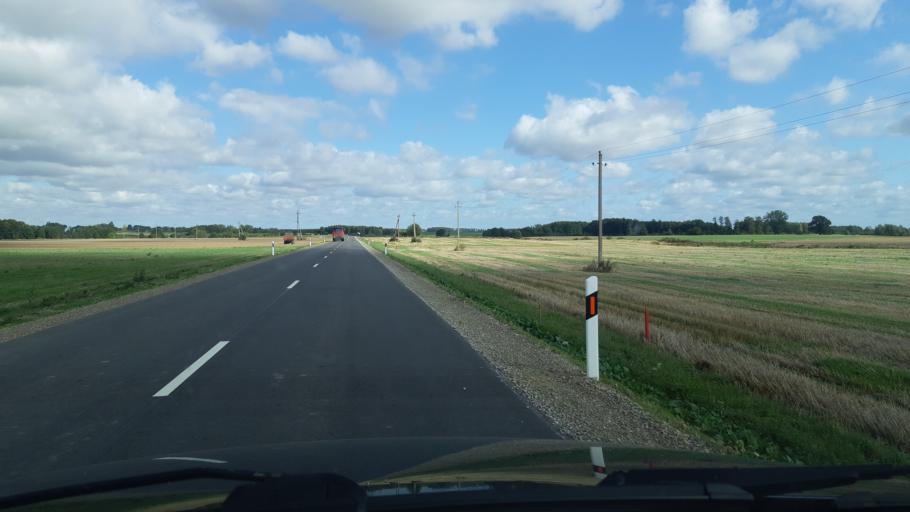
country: LT
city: Virbalis
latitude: 54.6366
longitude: 22.8330
